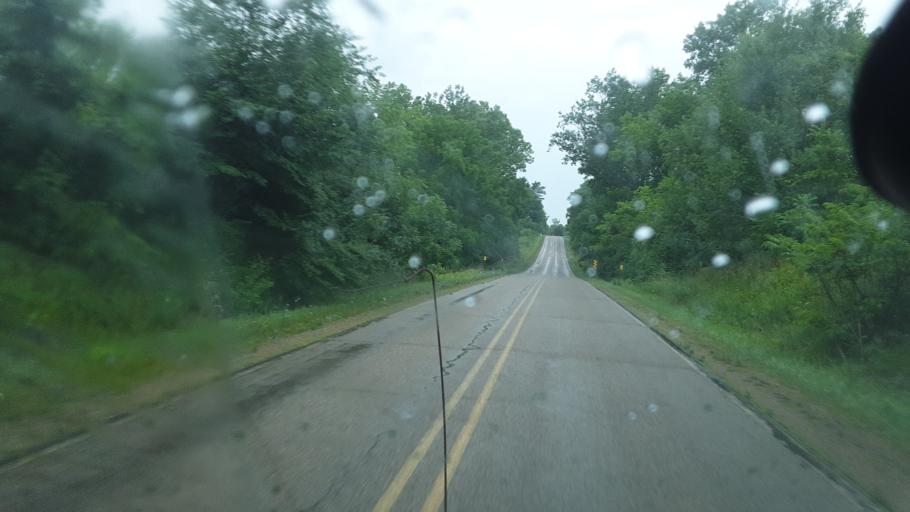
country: US
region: Michigan
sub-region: Hillsdale County
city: Reading
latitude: 41.7085
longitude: -84.7016
